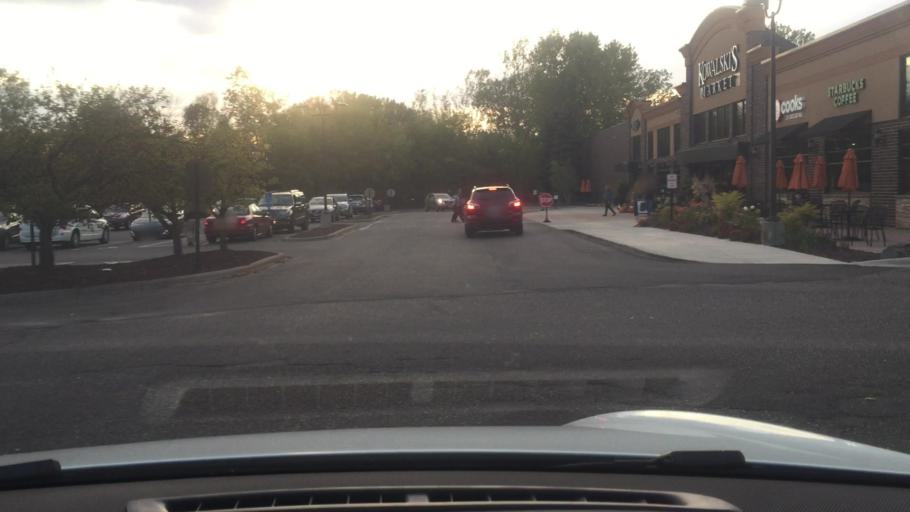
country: US
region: Minnesota
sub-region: Ramsey County
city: Shoreview
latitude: 45.0807
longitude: -93.1189
